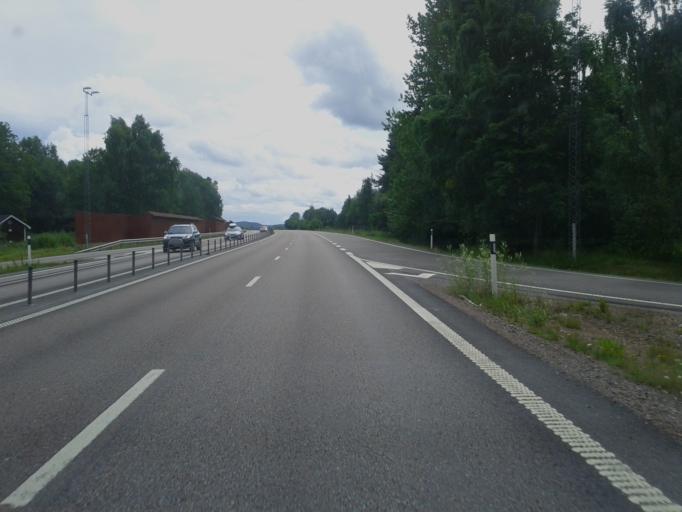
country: SE
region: Dalarna
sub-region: Borlange Kommun
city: Ornas
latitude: 60.4361
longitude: 15.5119
